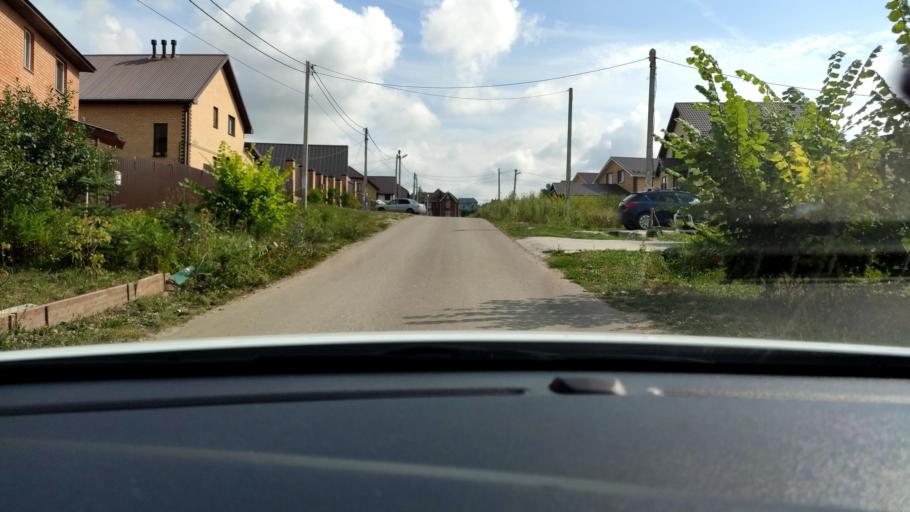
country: RU
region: Tatarstan
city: Stolbishchi
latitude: 55.7542
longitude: 49.2738
